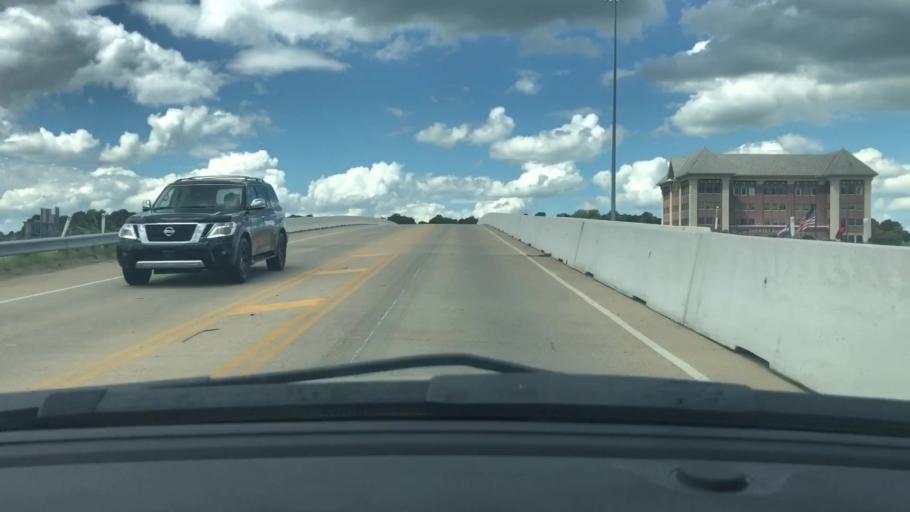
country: US
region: Arkansas
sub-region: Miller County
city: Texarkana
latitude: 33.4598
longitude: -94.0765
